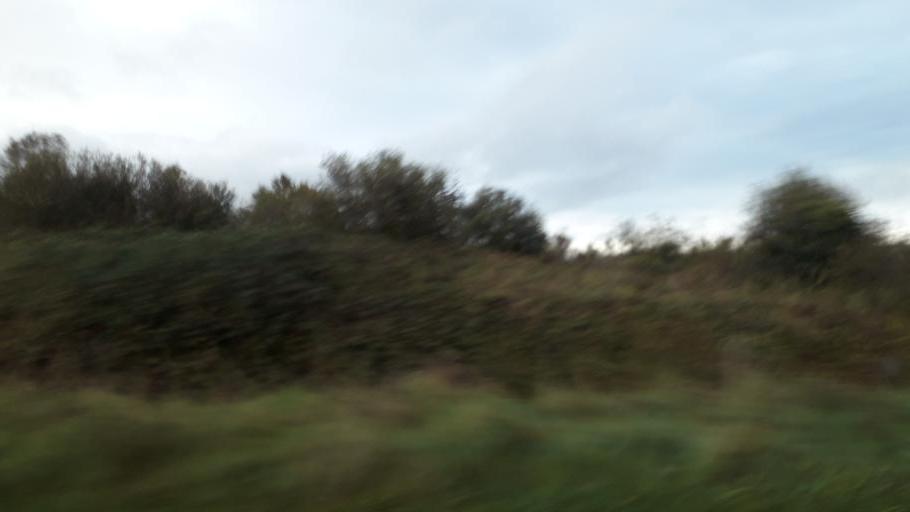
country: IE
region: Leinster
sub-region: An Longfort
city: Lanesborough
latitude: 53.7586
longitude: -7.9843
